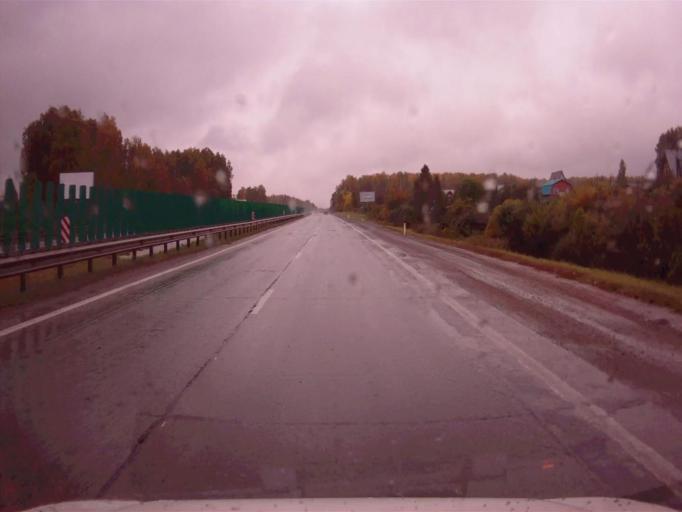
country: RU
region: Chelyabinsk
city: Dolgoderevenskoye
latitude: 55.3292
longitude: 61.3232
